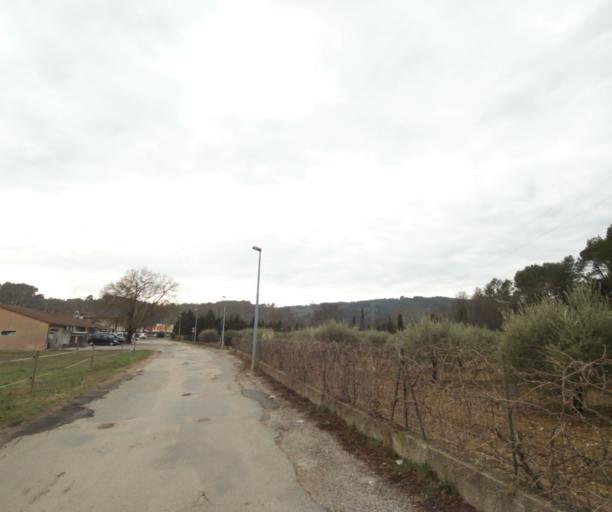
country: FR
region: Provence-Alpes-Cote d'Azur
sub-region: Departement du Var
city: Trans-en-Provence
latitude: 43.5116
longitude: 6.4812
